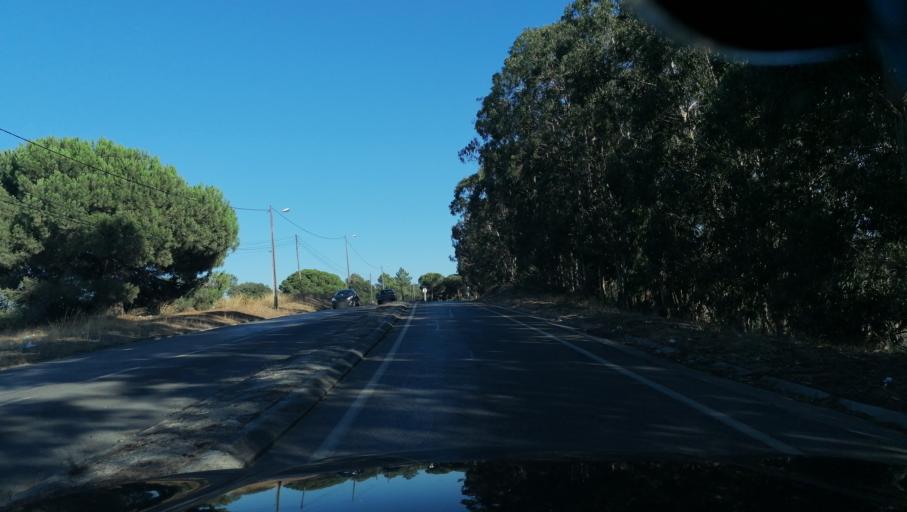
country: PT
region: Setubal
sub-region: Moita
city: Moita
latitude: 38.6316
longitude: -8.9682
